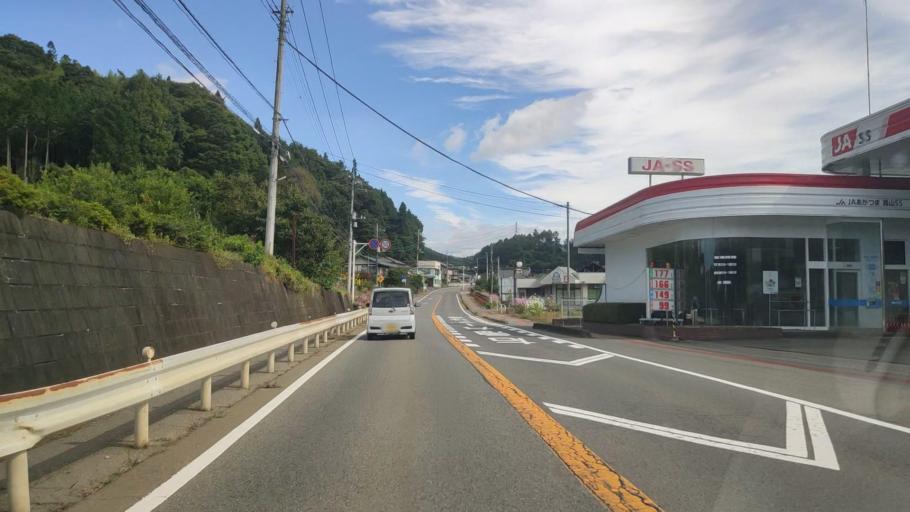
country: JP
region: Gunma
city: Nakanojomachi
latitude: 36.6200
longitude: 138.9402
